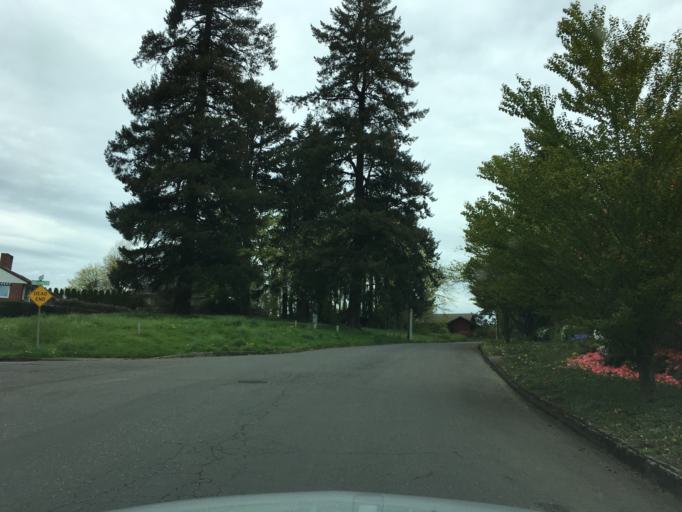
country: US
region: Oregon
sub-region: Multnomah County
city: Lents
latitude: 45.5201
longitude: -122.5967
